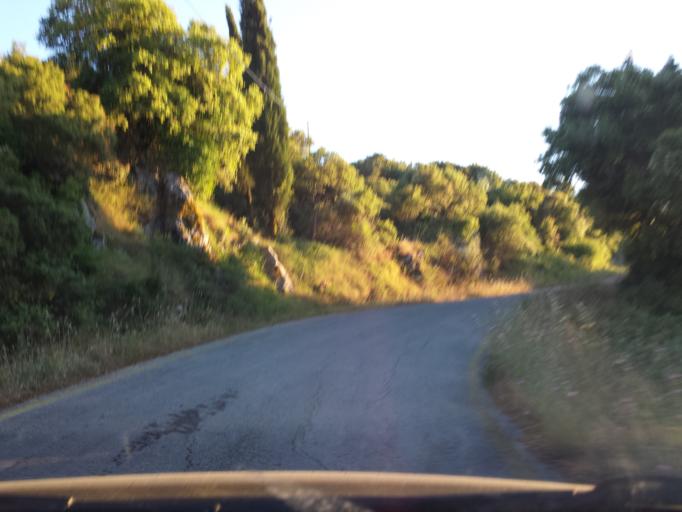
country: GR
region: Ionian Islands
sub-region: Nomos Kerkyras
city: Acharavi
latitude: 39.7459
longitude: 19.8377
